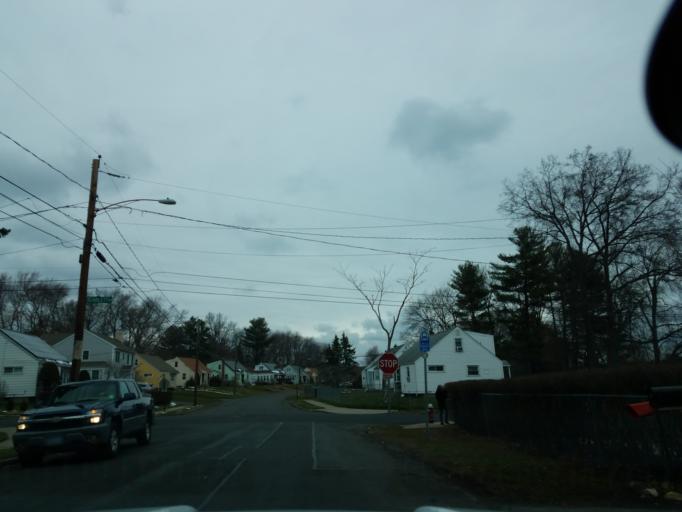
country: US
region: Connecticut
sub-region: Hartford County
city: Farmington
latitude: 41.6981
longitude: -72.7985
